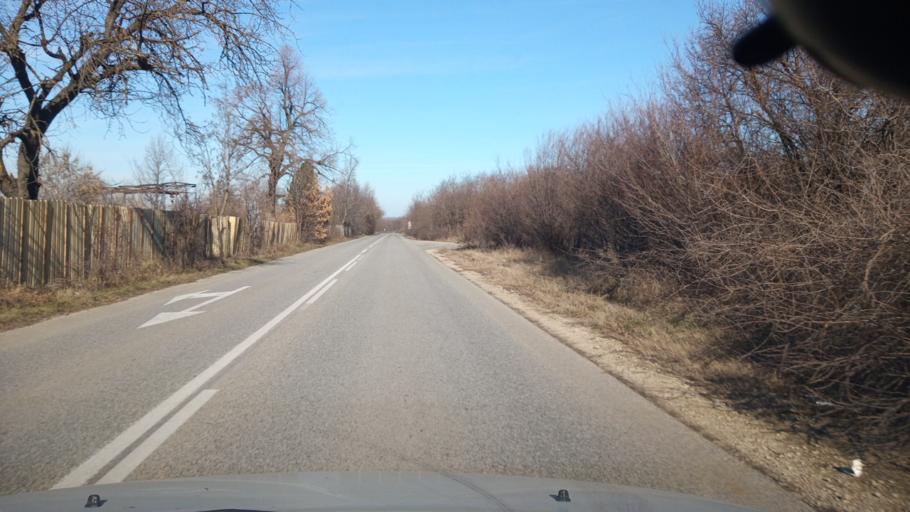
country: BG
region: Pleven
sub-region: Obshtina Pleven
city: Pleven
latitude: 43.4434
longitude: 24.7214
